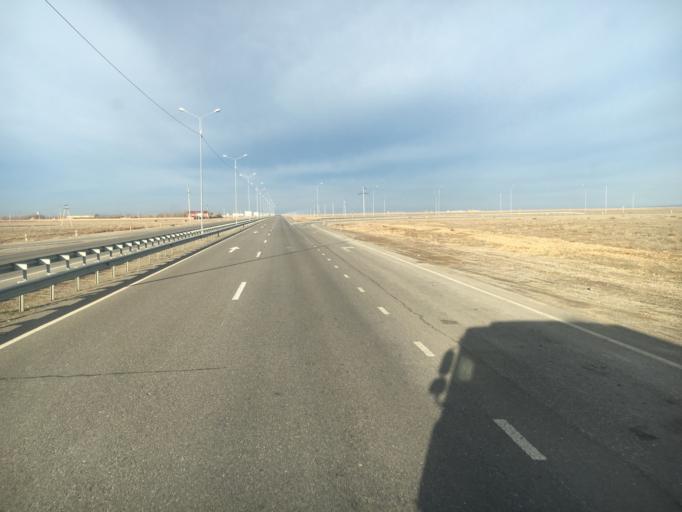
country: KZ
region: Ongtustik Qazaqstan
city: Turkestan
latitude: 43.4149
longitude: 68.0249
